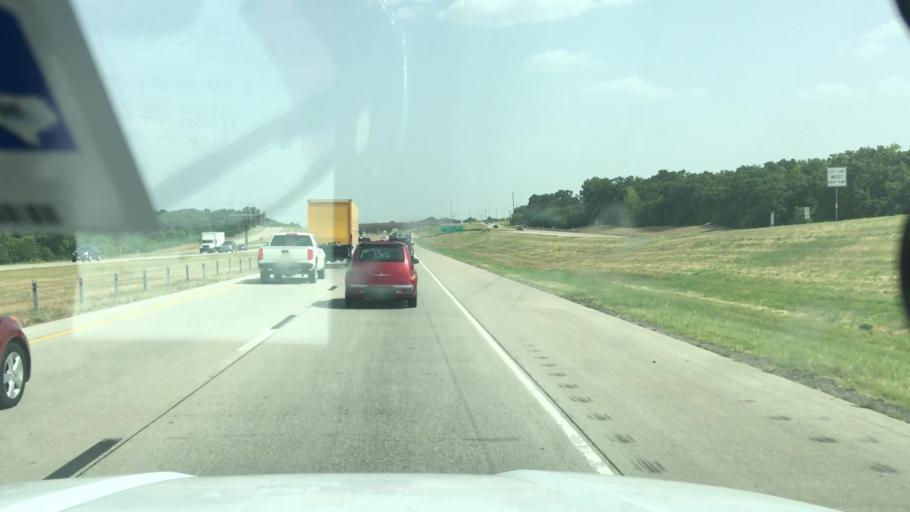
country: US
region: Texas
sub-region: Tarrant County
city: Grapevine
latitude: 32.8870
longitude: -97.0792
